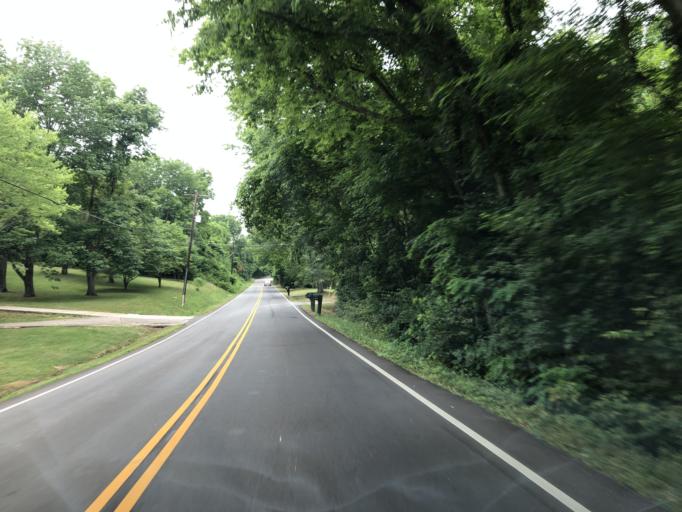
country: US
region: Tennessee
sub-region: Davidson County
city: Goodlettsville
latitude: 36.2966
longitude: -86.7587
